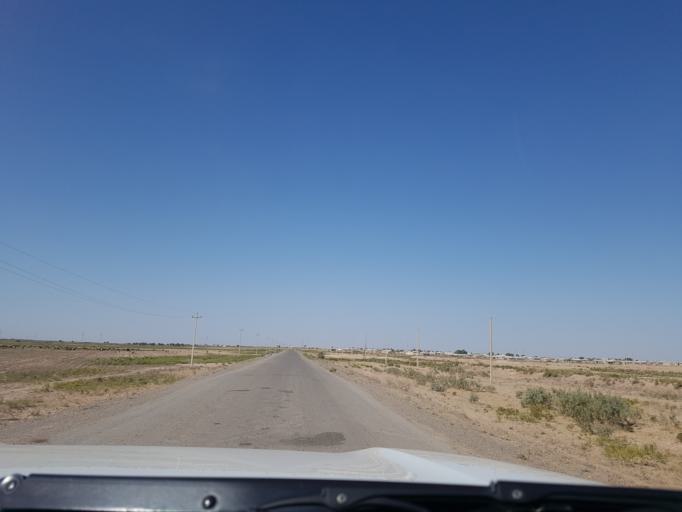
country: IR
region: Razavi Khorasan
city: Sarakhs
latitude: 36.5015
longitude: 61.2536
